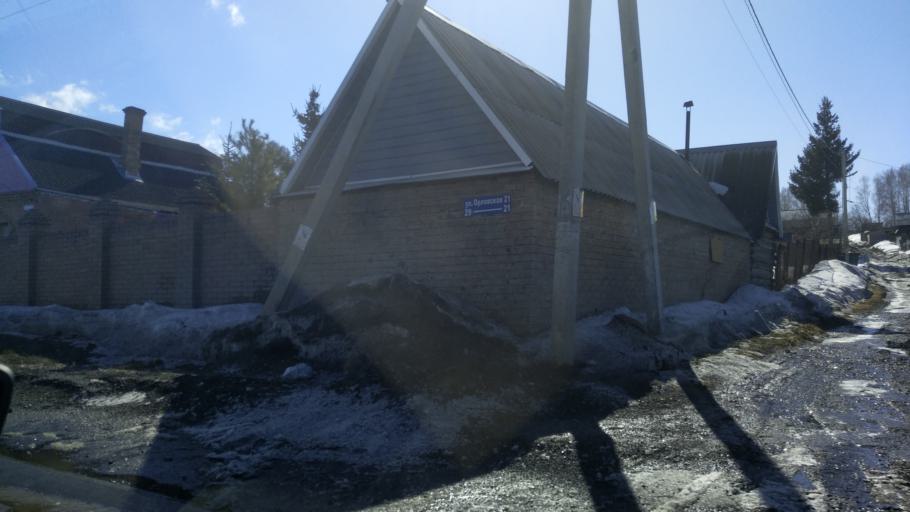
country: RU
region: Kemerovo
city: Yurga
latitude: 55.6984
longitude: 84.9689
